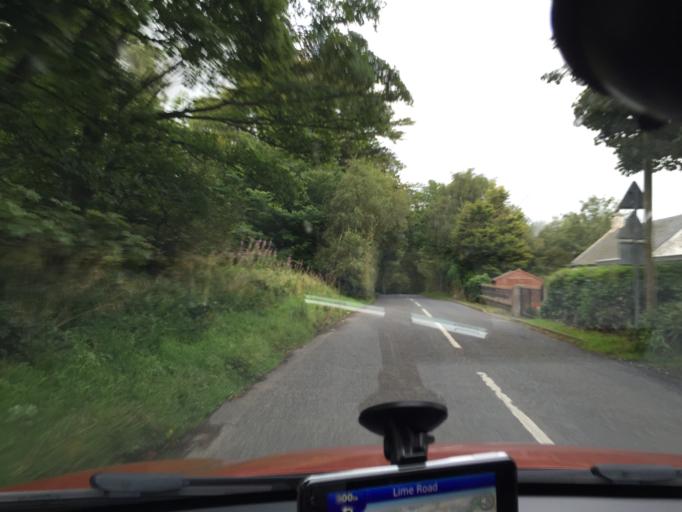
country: GB
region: Scotland
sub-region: Falkirk
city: Larbert
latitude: 55.9967
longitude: -3.8414
